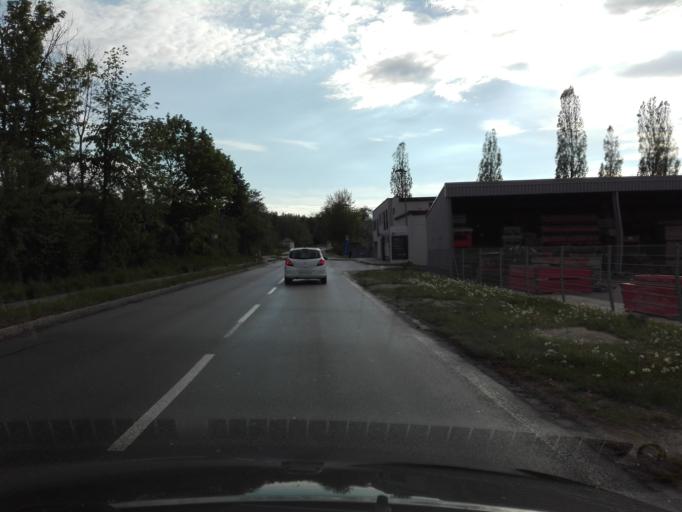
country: DE
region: Bavaria
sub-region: Lower Bavaria
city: Salzweg
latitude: 48.5736
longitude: 13.4971
